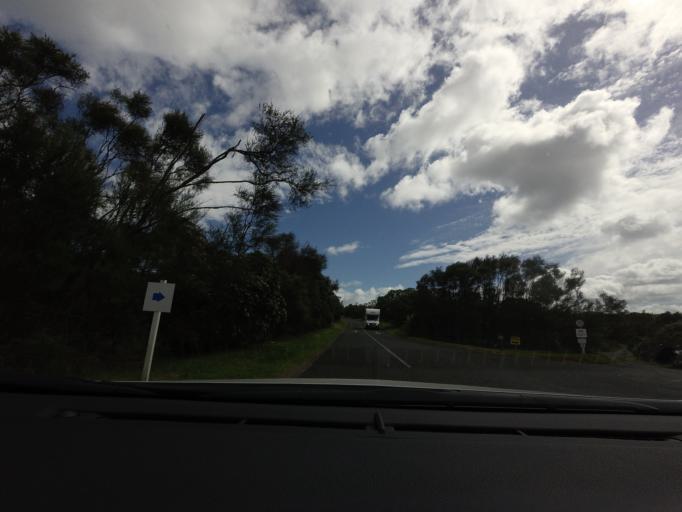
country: NZ
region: Bay of Plenty
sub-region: Rotorua District
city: Rotorua
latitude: -38.3517
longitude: 176.3684
